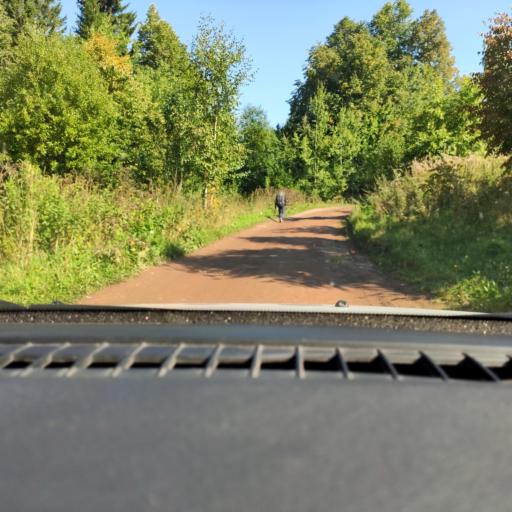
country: RU
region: Perm
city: Novyye Lyady
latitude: 58.0604
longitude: 56.5769
